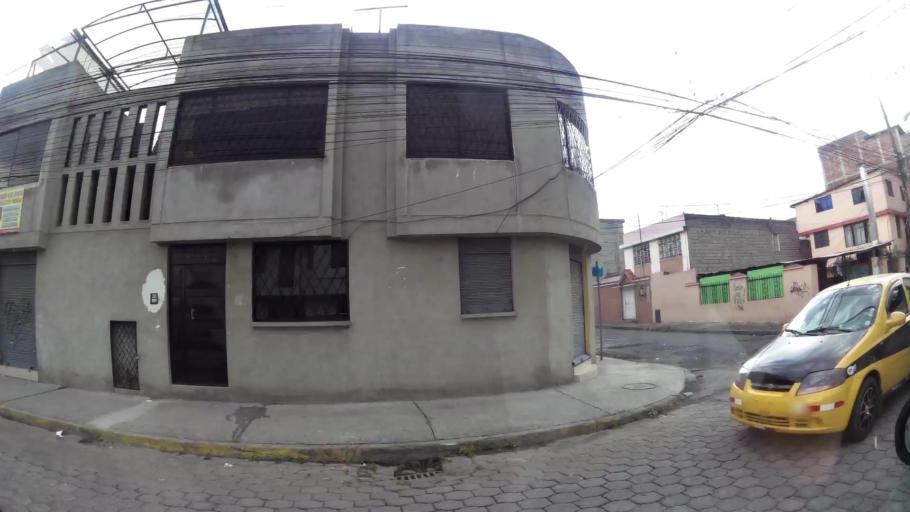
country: EC
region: Pichincha
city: Quito
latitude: -0.2824
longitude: -78.5385
